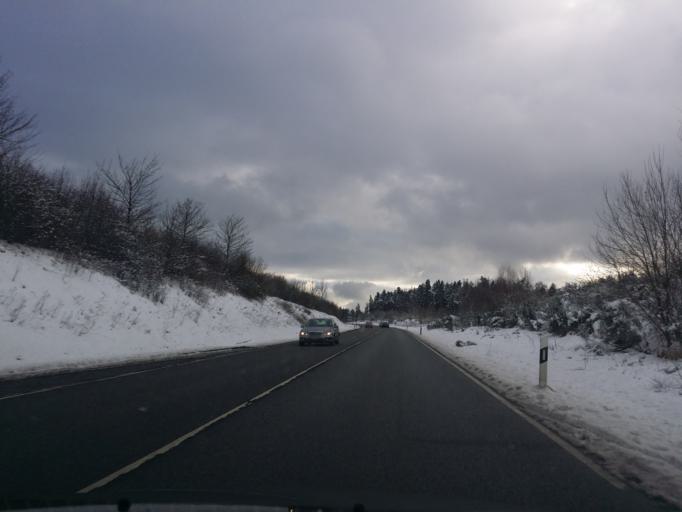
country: DE
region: Hesse
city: Taunusstein
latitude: 50.1566
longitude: 8.2120
